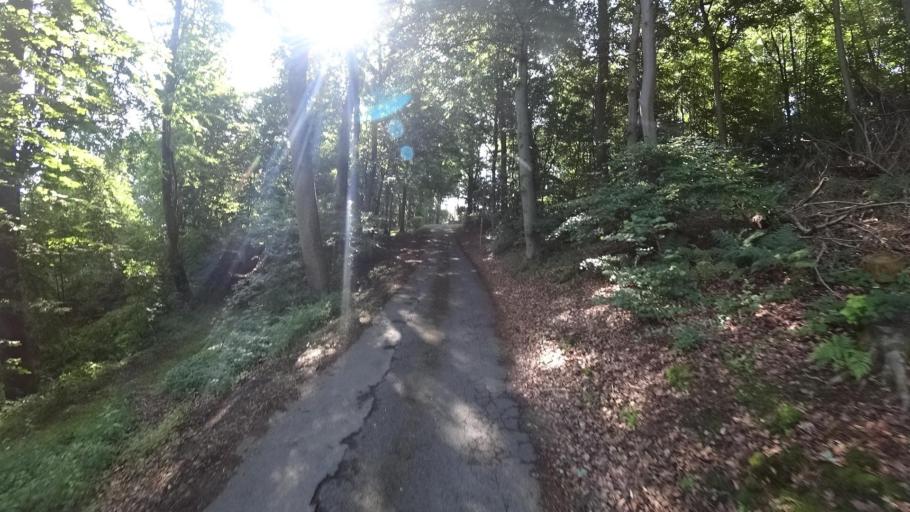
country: DE
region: Rheinland-Pfalz
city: Altenkirchen
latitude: 50.6818
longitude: 7.6501
